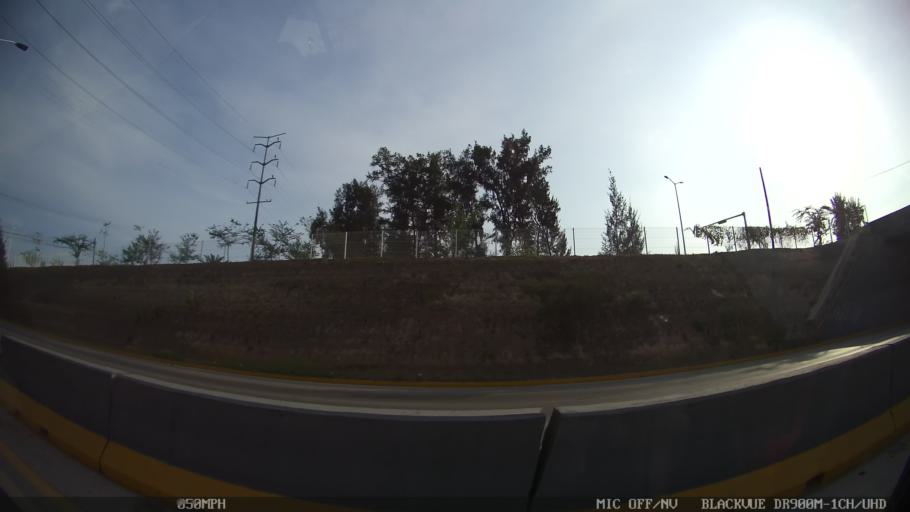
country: MX
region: Jalisco
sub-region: Zapopan
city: Zapopan
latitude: 20.7286
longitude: -103.3453
